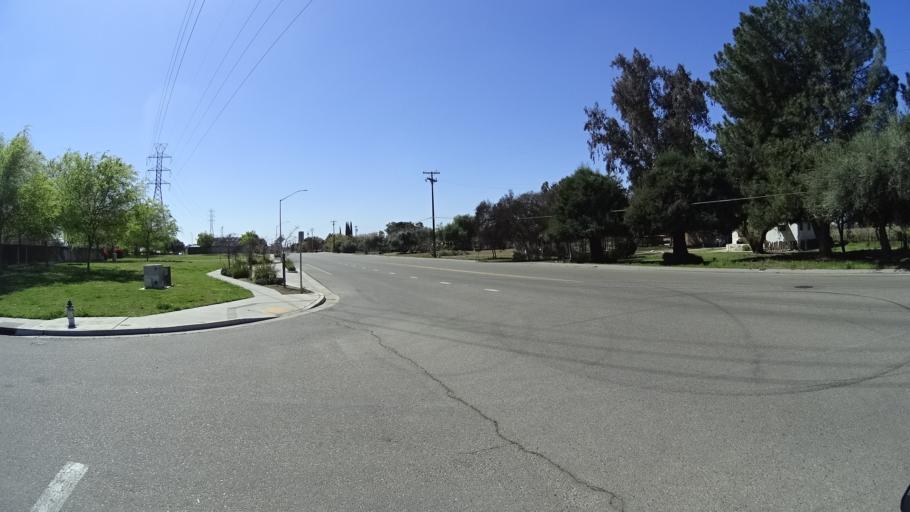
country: US
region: California
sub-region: Fresno County
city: West Park
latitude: 36.7851
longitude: -119.8982
